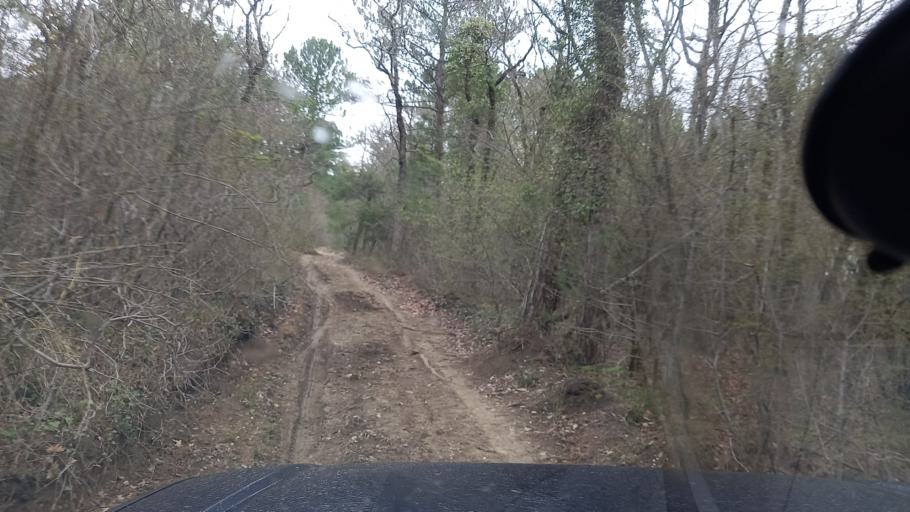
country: RU
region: Krasnodarskiy
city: Arkhipo-Osipovka
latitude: 44.3711
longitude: 38.4726
